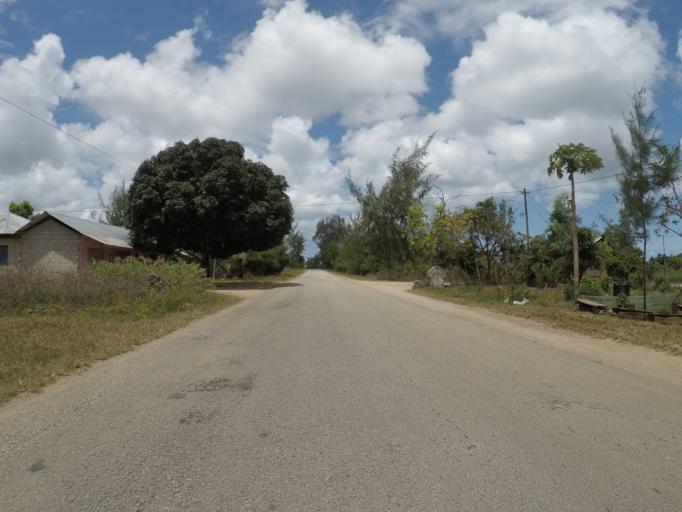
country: TZ
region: Zanzibar Central/South
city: Mahonda
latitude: -6.3108
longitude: 39.4320
